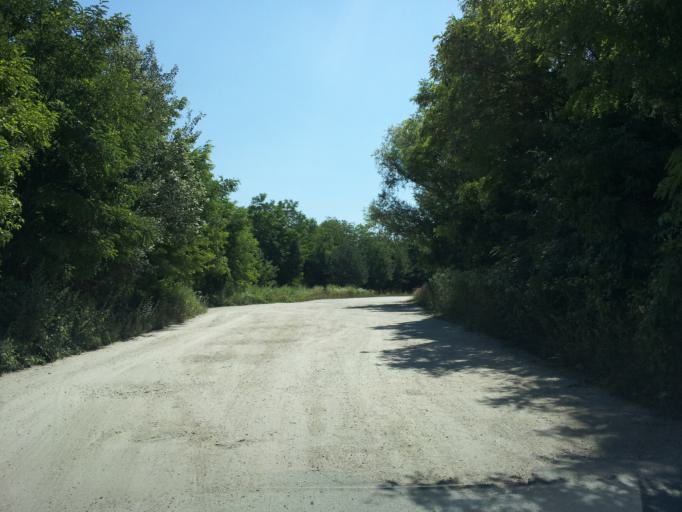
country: HU
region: Fejer
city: Szarliget
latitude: 47.5304
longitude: 18.5578
